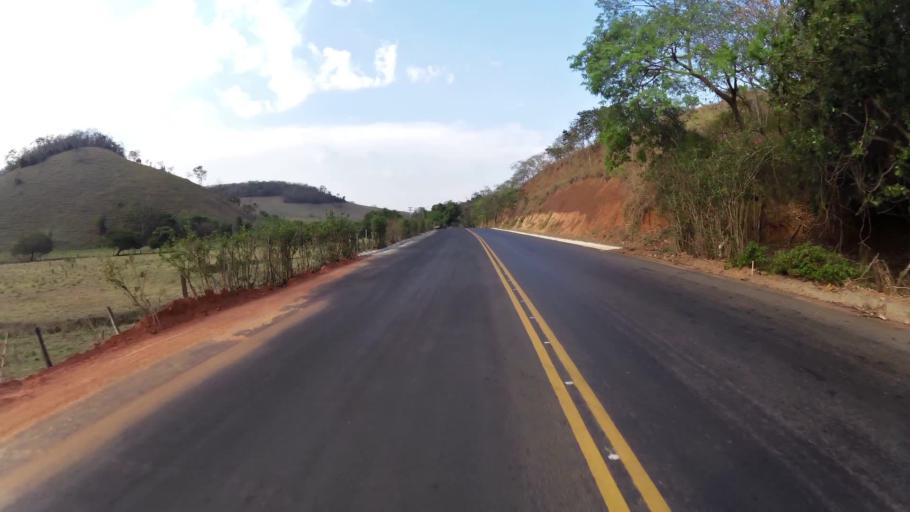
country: BR
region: Rio de Janeiro
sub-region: Santo Antonio De Padua
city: Santo Antonio de Padua
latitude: -21.4853
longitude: -42.0577
